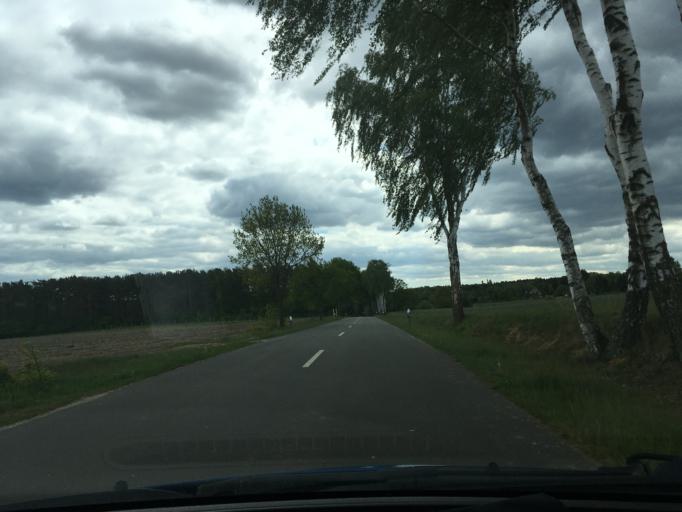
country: DE
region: Lower Saxony
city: Suderburg
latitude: 52.8648
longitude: 10.4137
